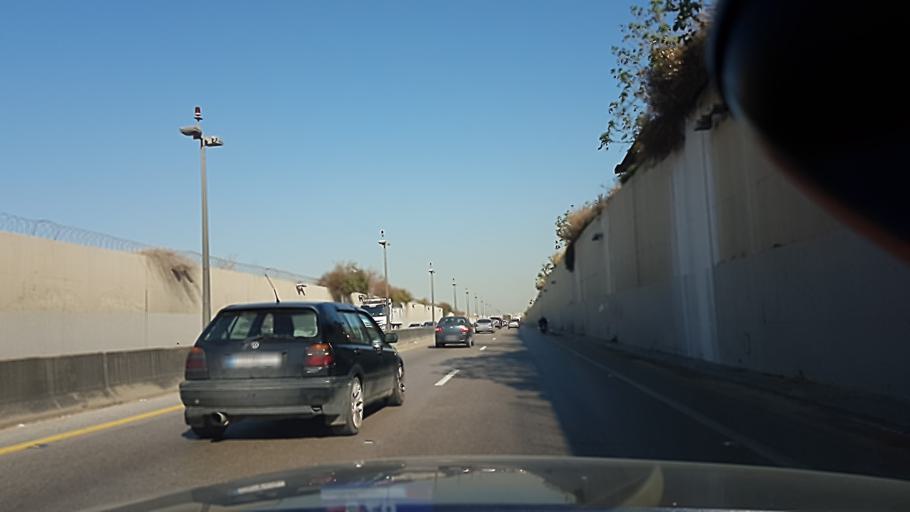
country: LB
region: Mont-Liban
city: Baabda
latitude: 33.8026
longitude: 35.4867
